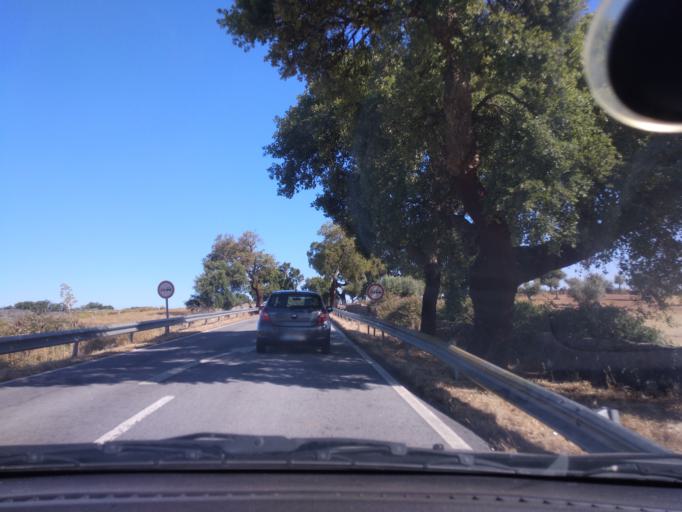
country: PT
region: Portalegre
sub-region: Nisa
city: Nisa
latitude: 39.4926
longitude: -7.6399
